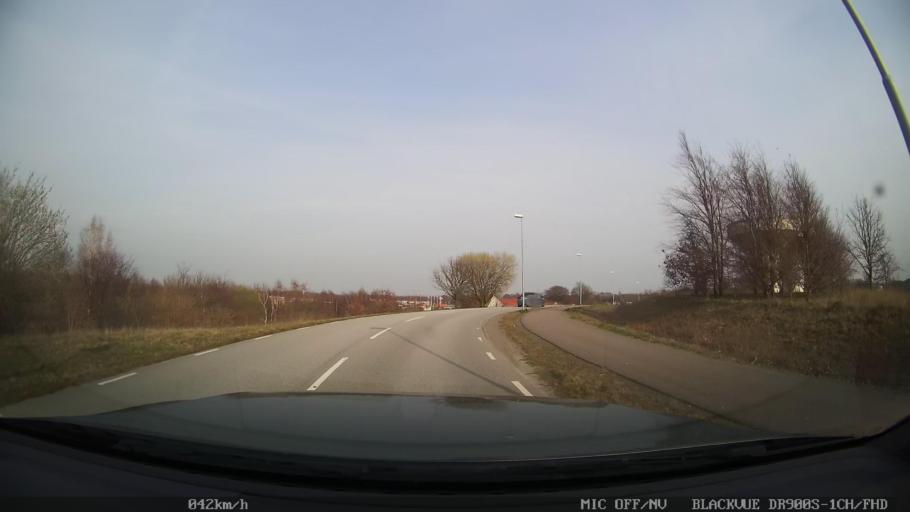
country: SE
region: Skane
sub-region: Ystads Kommun
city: Ystad
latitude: 55.4433
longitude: 13.8015
